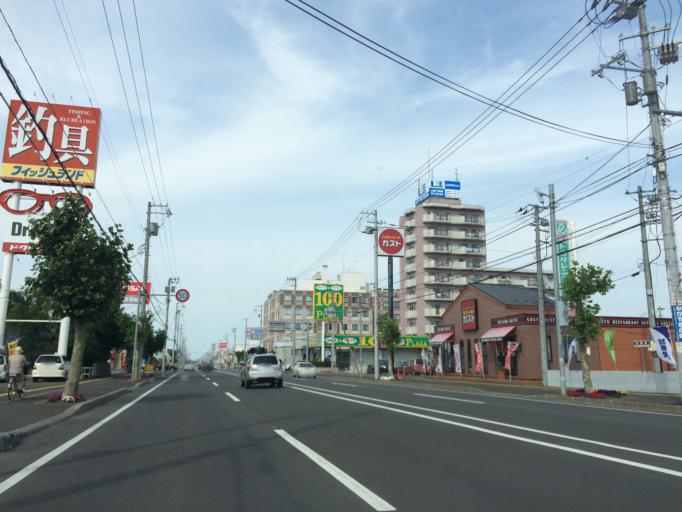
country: JP
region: Hokkaido
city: Ebetsu
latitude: 43.1001
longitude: 141.5335
